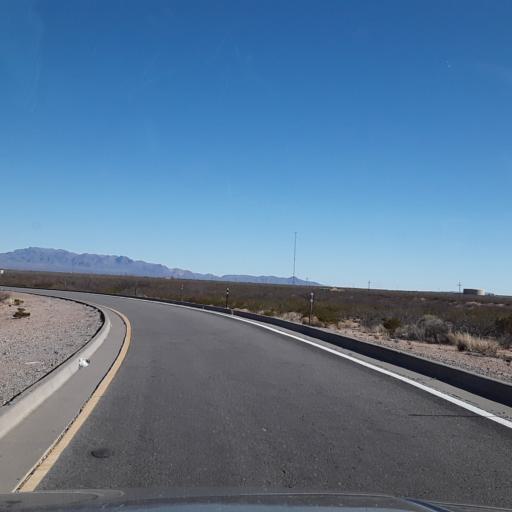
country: US
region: New Mexico
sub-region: Dona Ana County
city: Mesilla
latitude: 32.2802
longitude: -106.8862
